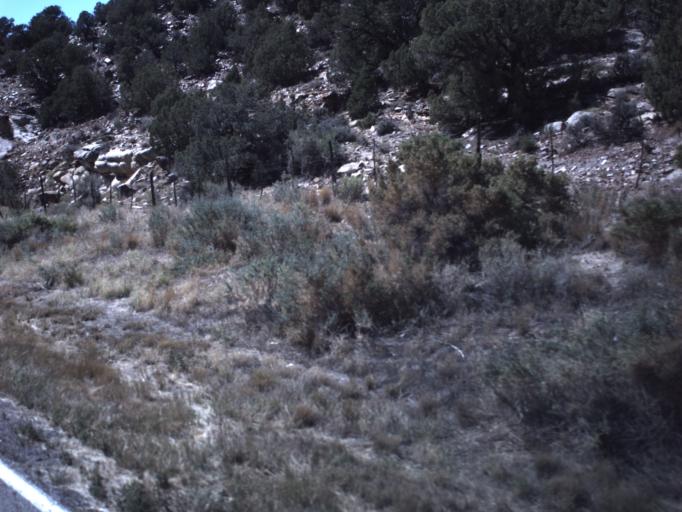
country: US
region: Utah
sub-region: Grand County
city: Moab
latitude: 38.3107
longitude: -109.3555
